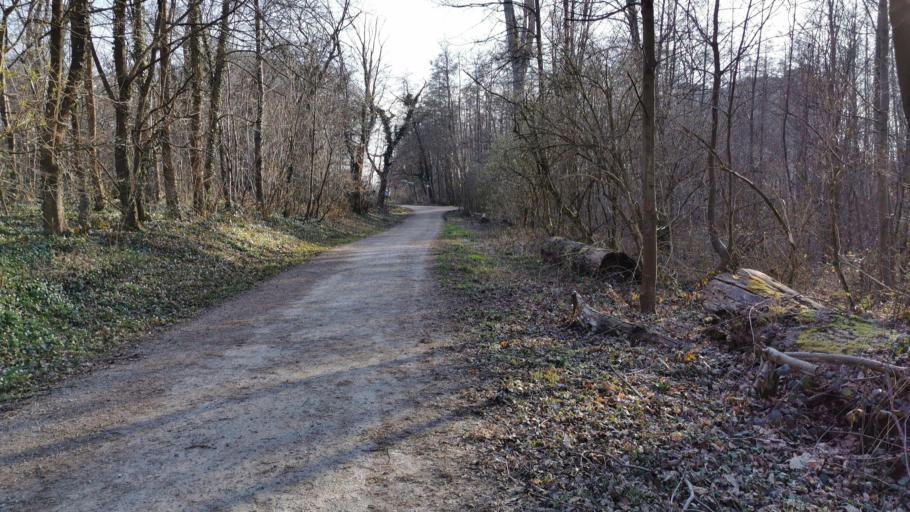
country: DE
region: Baden-Wuerttemberg
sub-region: Karlsruhe Region
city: Karlsruhe
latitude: 48.9844
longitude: 8.4098
